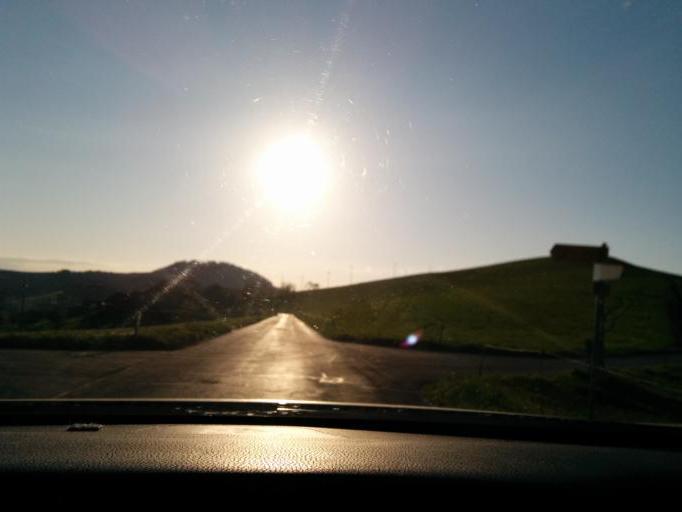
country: CH
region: Bern
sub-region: Bern-Mittelland District
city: Rueggisberg
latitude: 46.8366
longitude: 7.4196
